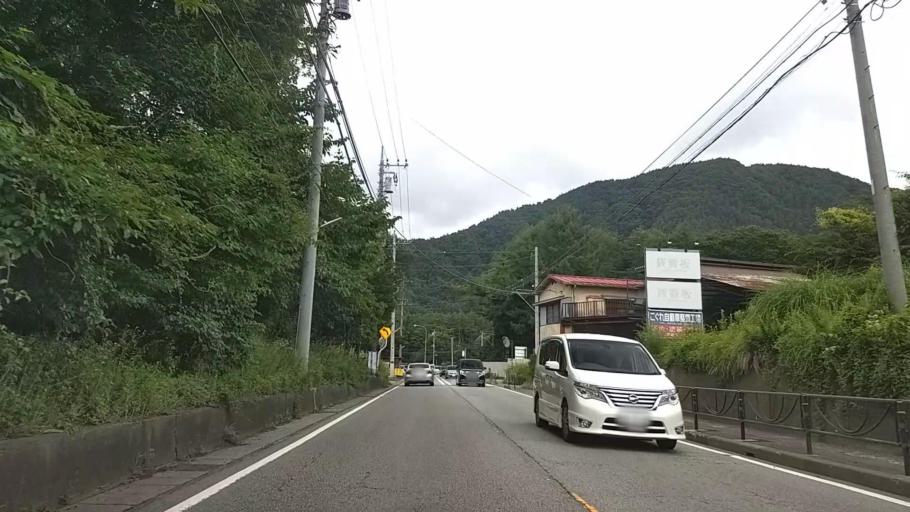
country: JP
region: Yamanashi
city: Fujikawaguchiko
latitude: 35.4843
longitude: 138.7203
